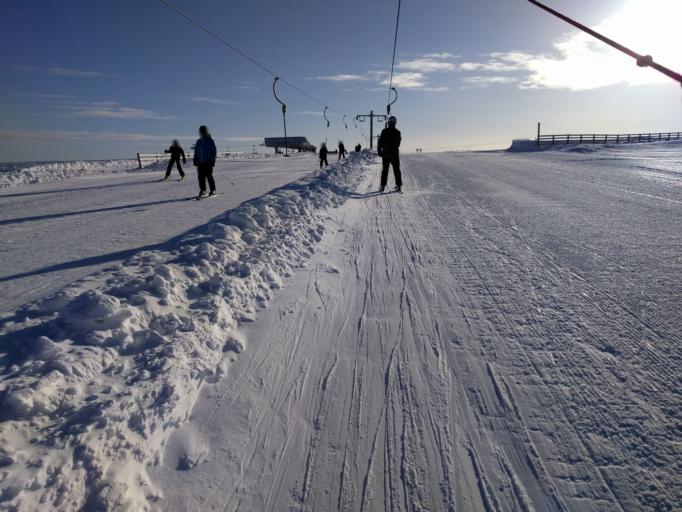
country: NO
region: Hedmark
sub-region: Trysil
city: Innbygda
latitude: 61.1745
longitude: 13.0202
